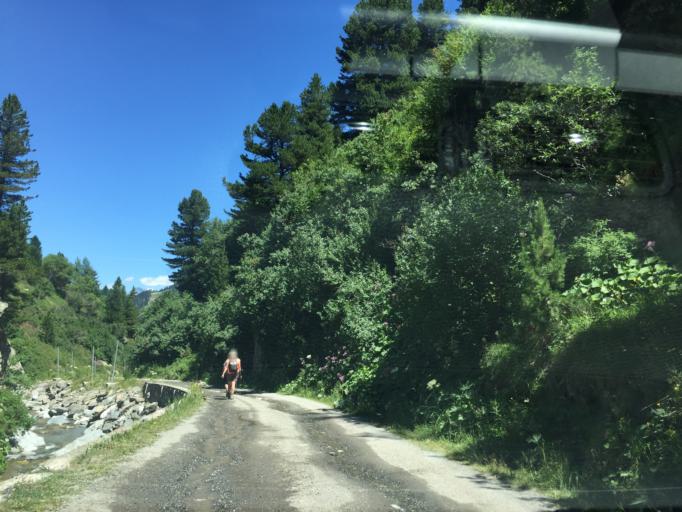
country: FR
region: Rhone-Alpes
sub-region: Departement de la Savoie
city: Modane
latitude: 45.1494
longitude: 6.6349
